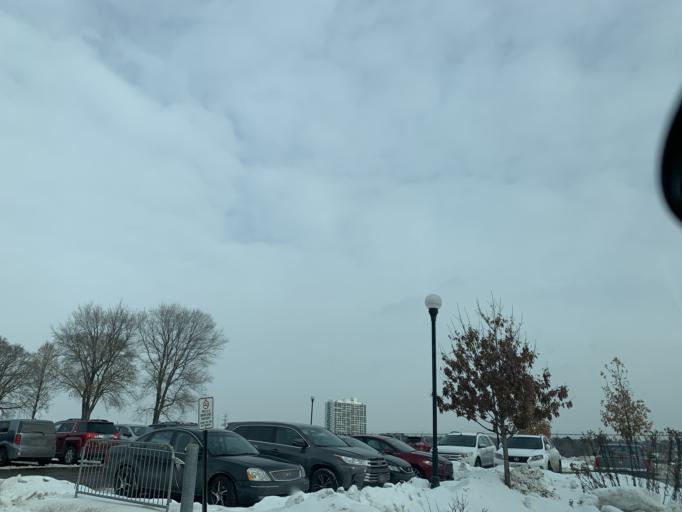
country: US
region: Minnesota
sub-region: Dakota County
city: Mendota Heights
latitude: 44.9145
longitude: -93.2039
